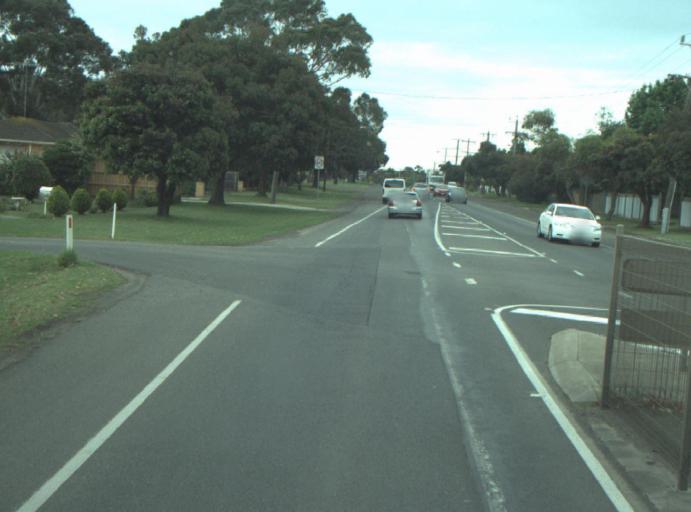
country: AU
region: Victoria
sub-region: Greater Geelong
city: Clifton Springs
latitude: -38.1789
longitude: 144.5602
